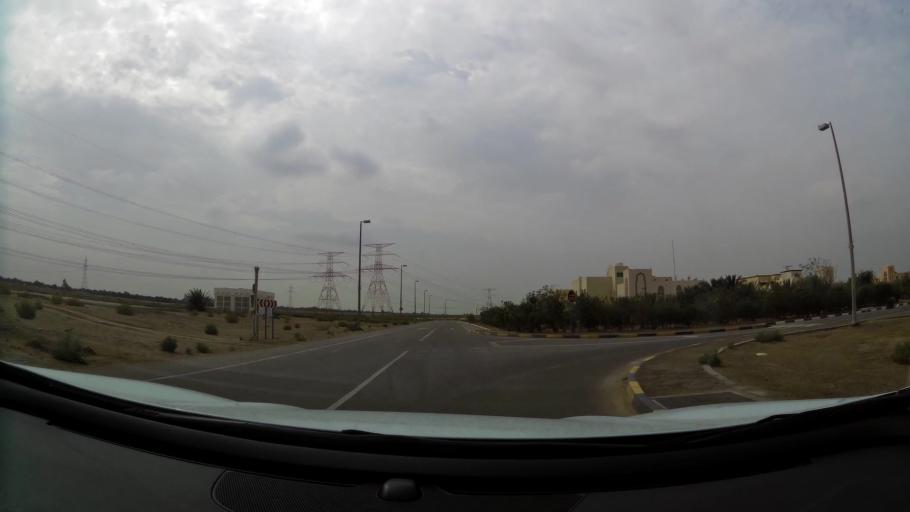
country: AE
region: Abu Dhabi
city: Abu Dhabi
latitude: 24.6323
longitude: 54.6924
